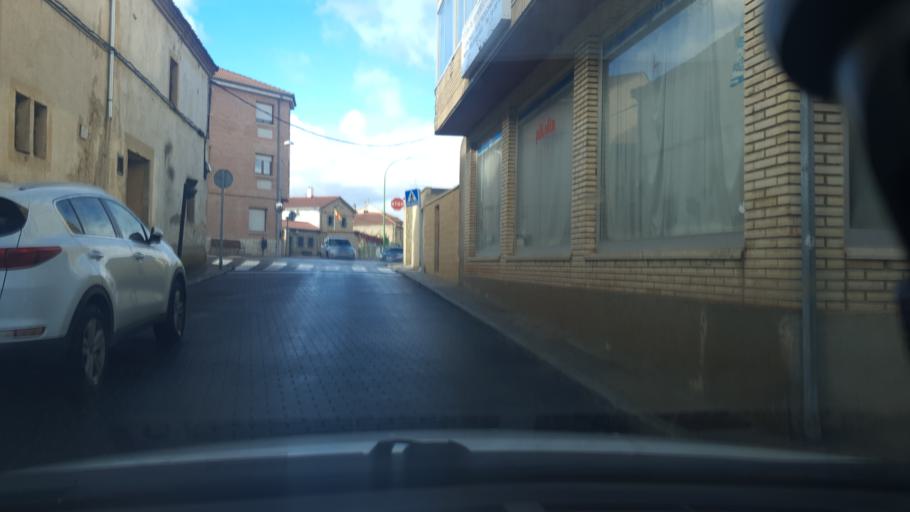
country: ES
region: Castille and Leon
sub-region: Provincia de Segovia
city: Carbonero el Mayor
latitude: 41.1228
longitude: -4.2681
